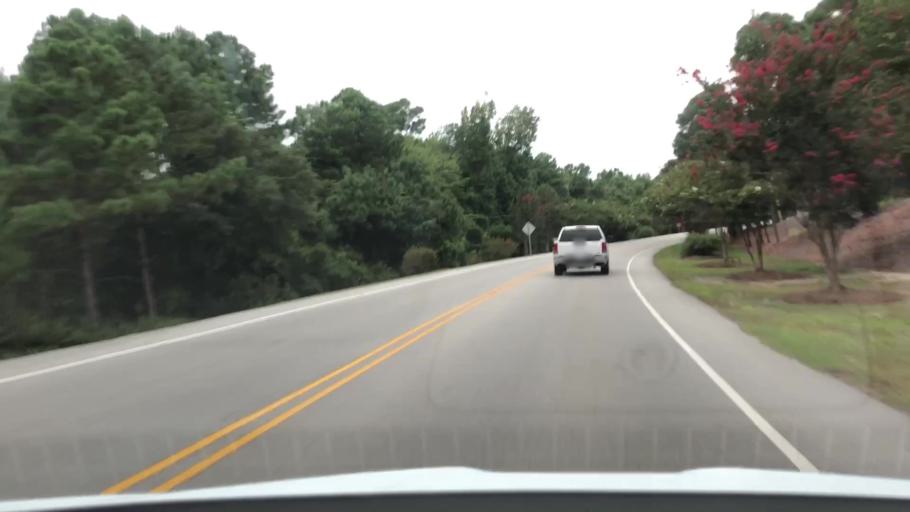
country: US
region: North Carolina
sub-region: Carteret County
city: Cedar Point
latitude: 34.6622
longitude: -77.0613
